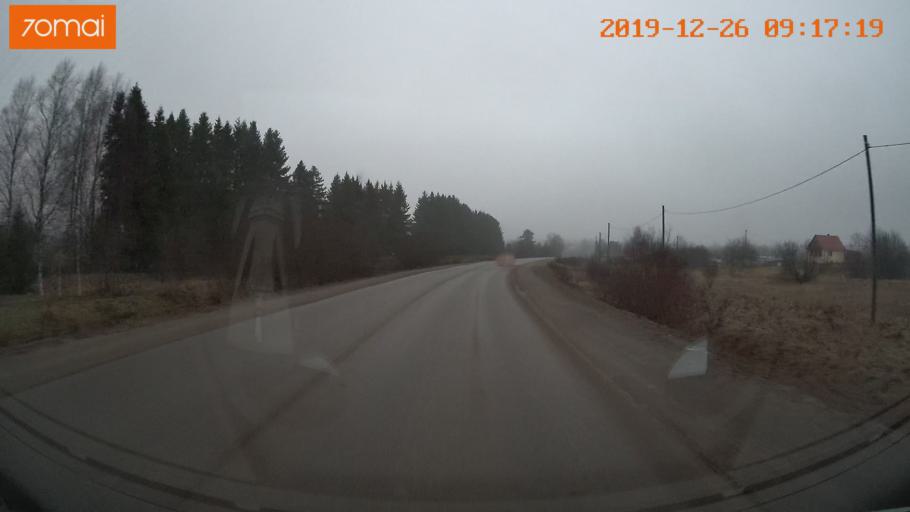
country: RU
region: Vologda
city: Gryazovets
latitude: 58.9283
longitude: 40.2385
